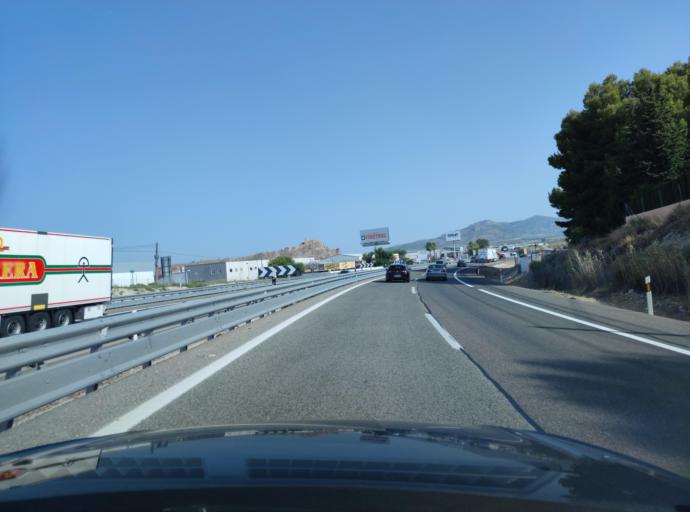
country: ES
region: Valencia
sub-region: Provincia de Alicante
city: Sax
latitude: 38.5275
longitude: -0.8071
